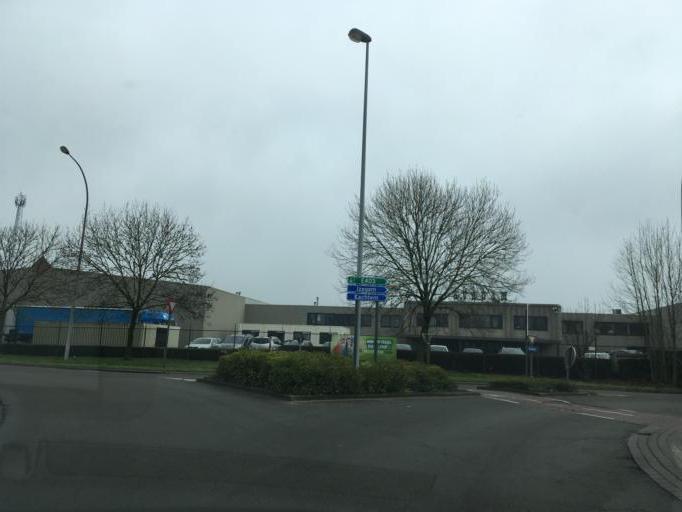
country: BE
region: Flanders
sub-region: Provincie West-Vlaanderen
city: Roeselare
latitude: 50.9461
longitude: 3.1522
